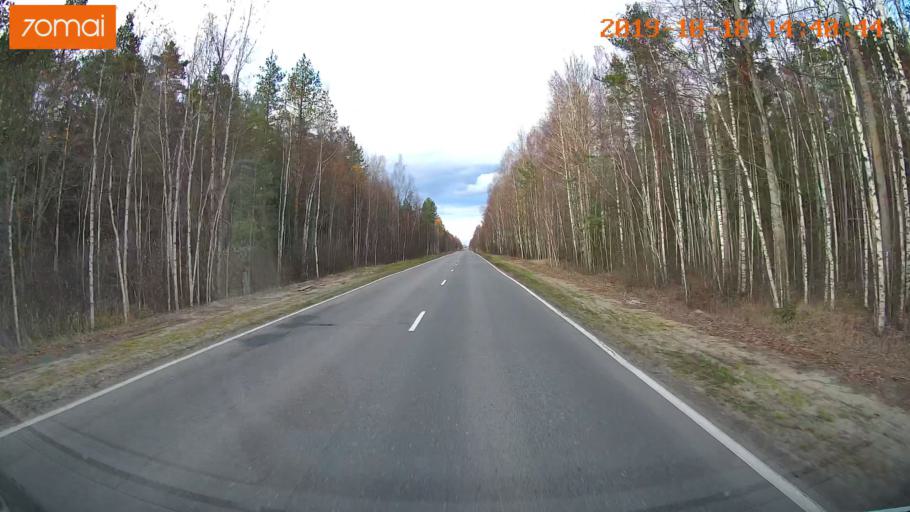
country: RU
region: Vladimir
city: Velikodvorskiy
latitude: 55.2811
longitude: 40.6695
